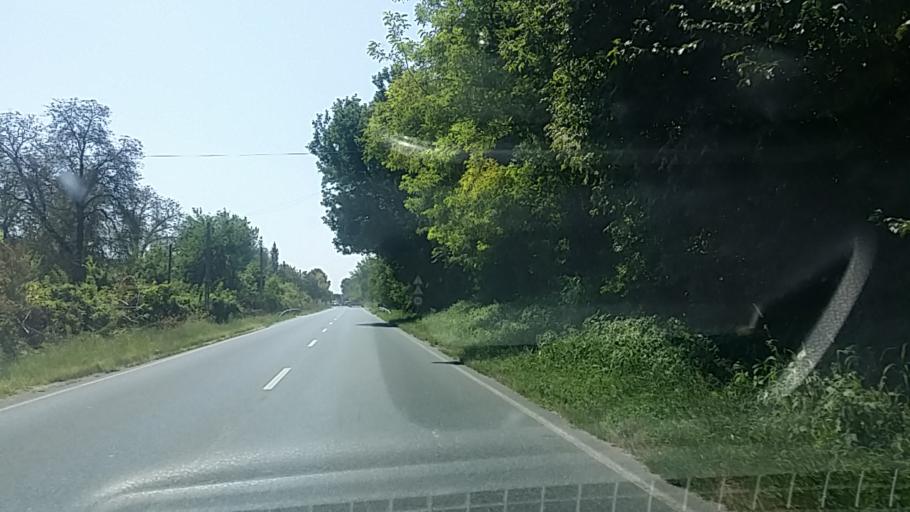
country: HU
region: Tolna
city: Paks
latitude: 46.6438
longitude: 18.8794
